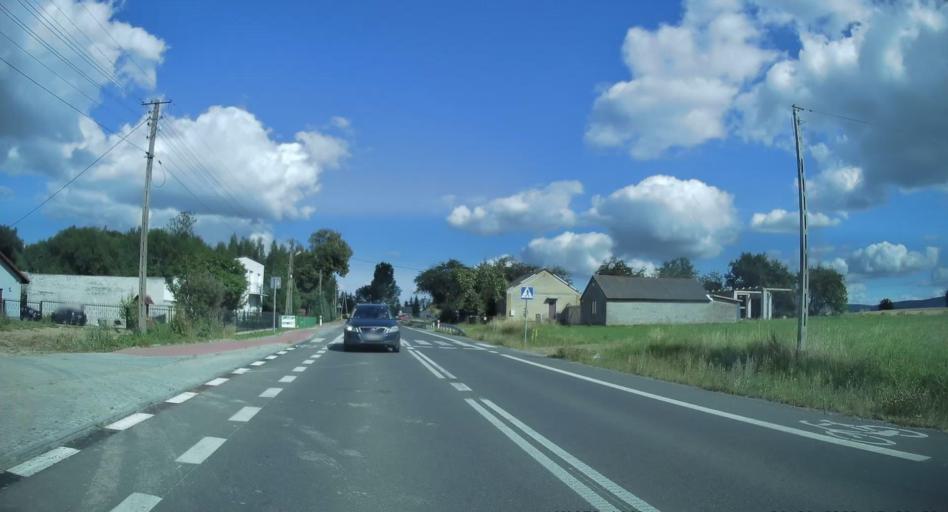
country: PL
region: Swietokrzyskie
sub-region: Powiat kielecki
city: Bodzentyn
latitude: 50.9312
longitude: 20.9761
